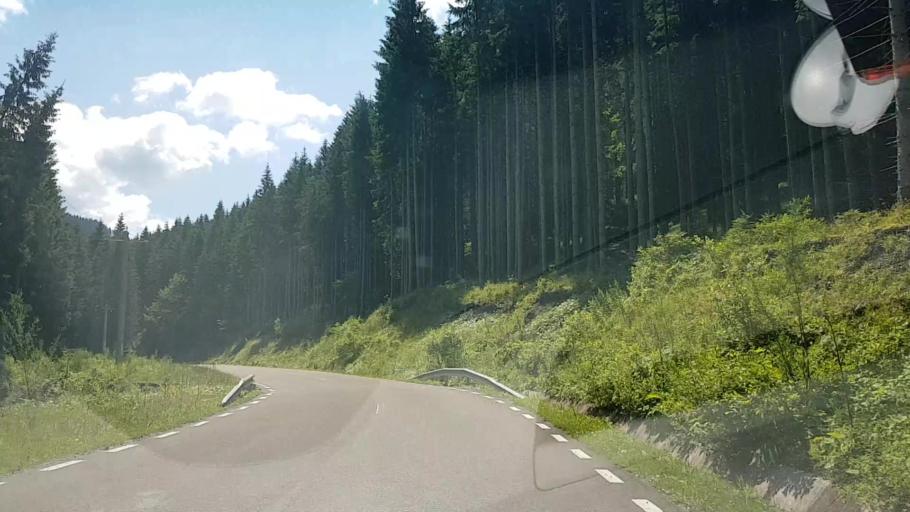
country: RO
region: Suceava
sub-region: Comuna Sadova
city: Sadova
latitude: 47.4742
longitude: 25.5026
